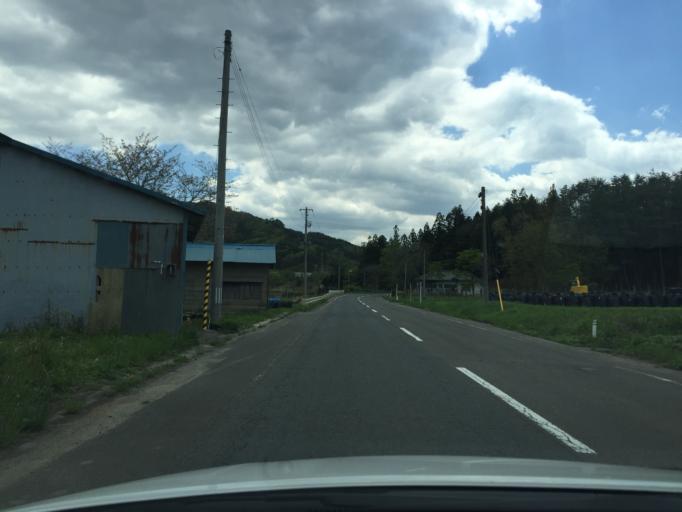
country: JP
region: Fukushima
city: Yanagawamachi-saiwaicho
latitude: 37.7191
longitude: 140.6898
